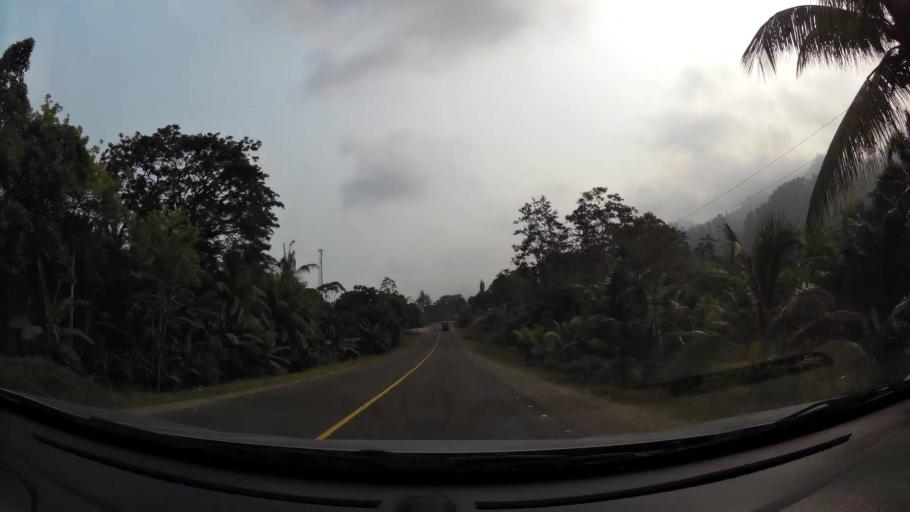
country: HN
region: Atlantida
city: Mezapa
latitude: 15.5822
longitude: -87.6126
